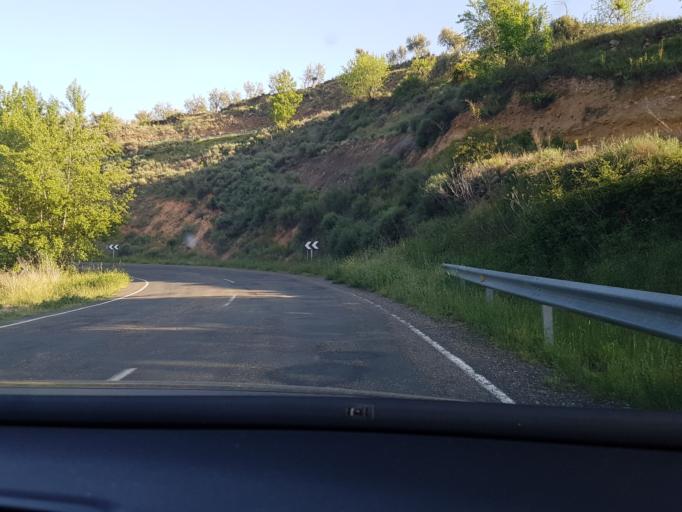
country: ES
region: La Rioja
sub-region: Provincia de La Rioja
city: Santa Eulalia Bajera
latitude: 42.2059
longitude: -2.1907
